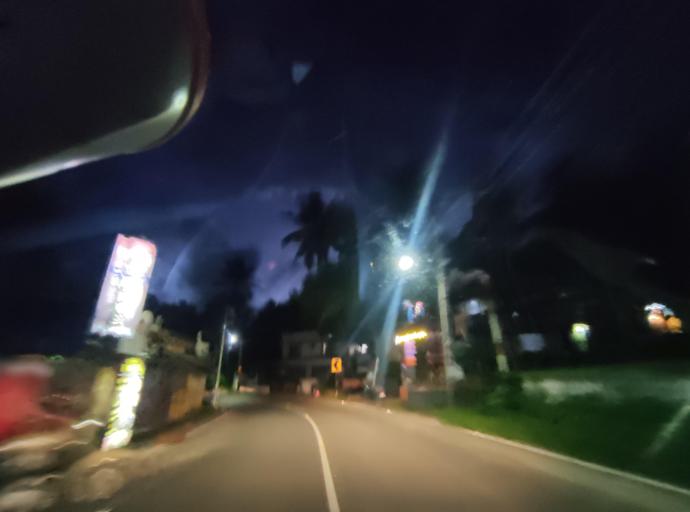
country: IN
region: Kerala
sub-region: Thiruvananthapuram
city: Nedumangad
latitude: 8.5596
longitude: 76.9593
